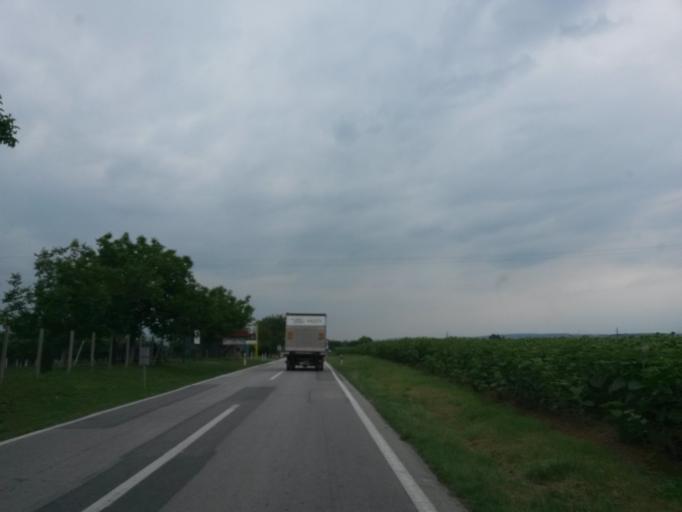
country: HR
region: Vukovarsko-Srijemska
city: Ilok
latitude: 45.2285
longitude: 19.3288
